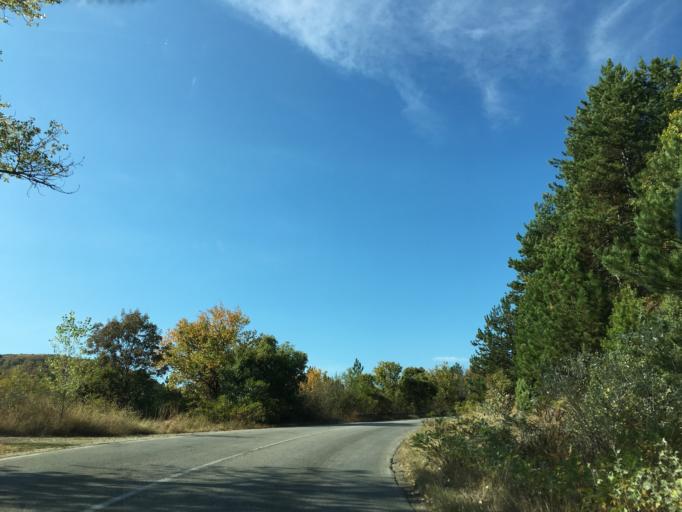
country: BG
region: Khaskovo
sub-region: Obshtina Ivaylovgrad
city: Ivaylovgrad
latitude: 41.5256
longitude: 26.1066
